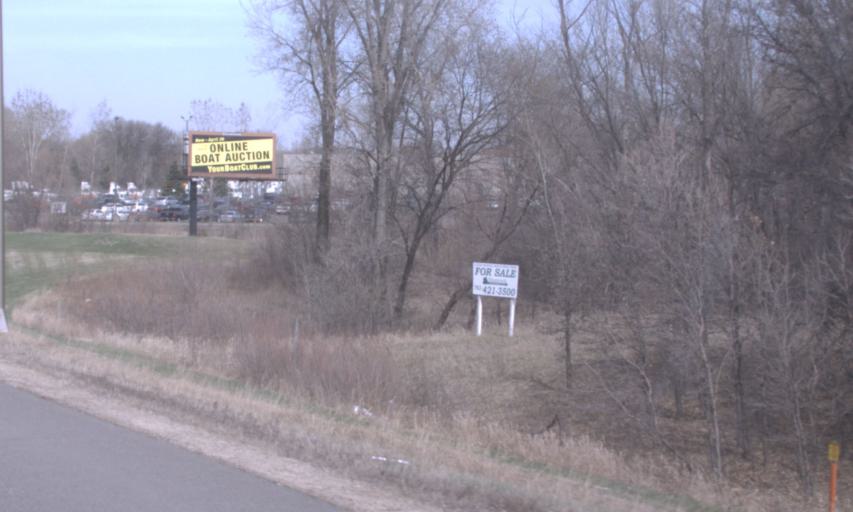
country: US
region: Minnesota
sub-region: Anoka County
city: Coon Rapids
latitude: 45.1718
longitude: -93.2970
